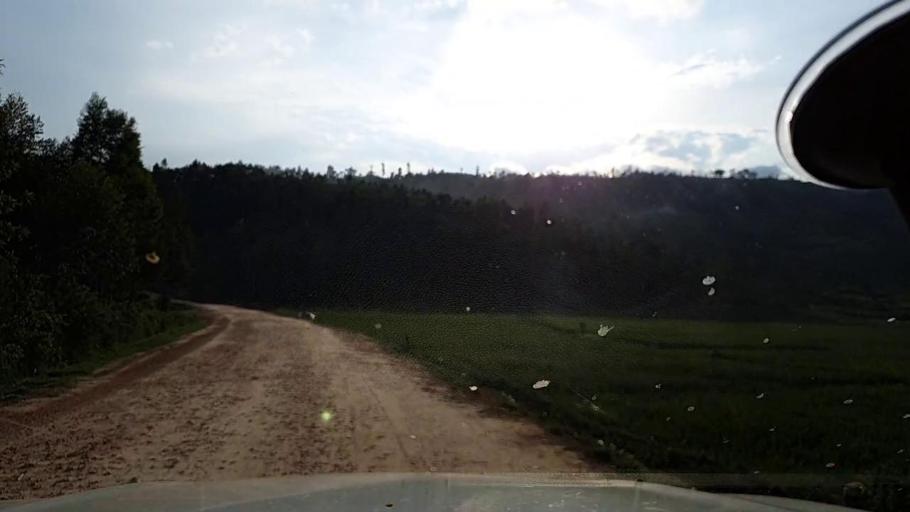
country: RW
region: Southern Province
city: Gitarama
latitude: -2.1964
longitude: 29.5778
